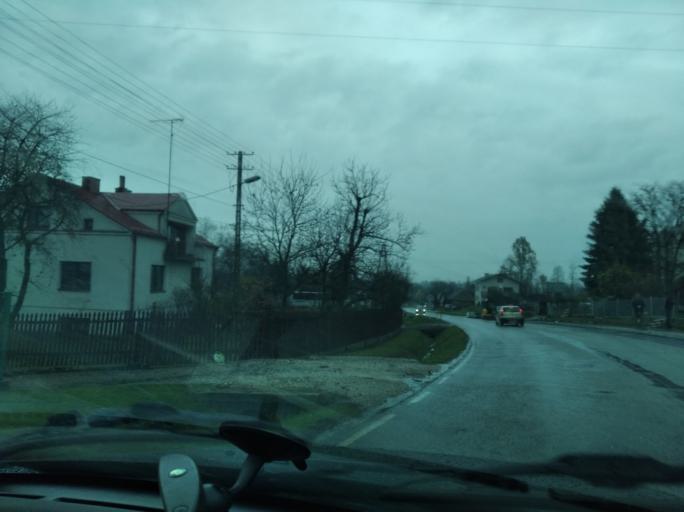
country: PL
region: Subcarpathian Voivodeship
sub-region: Powiat lancucki
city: Albigowa
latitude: 50.0125
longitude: 22.2231
